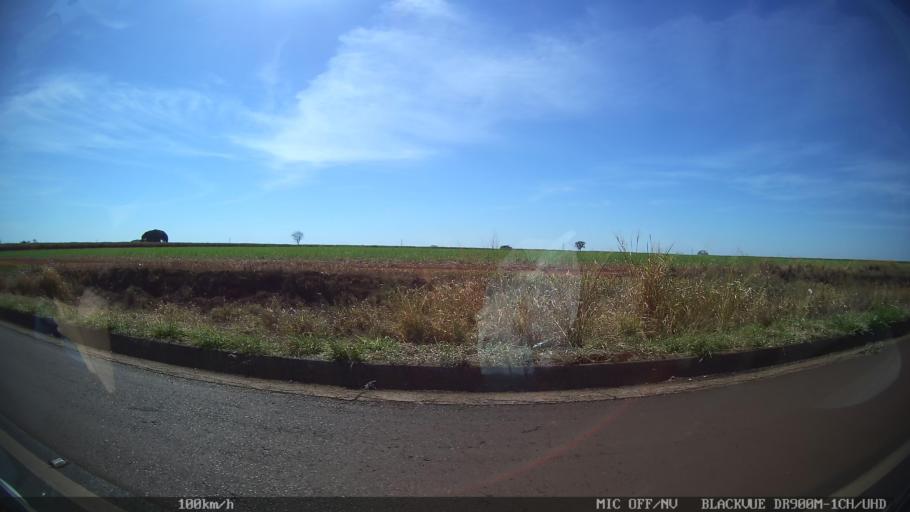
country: BR
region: Sao Paulo
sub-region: Ipua
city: Ipua
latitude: -20.4778
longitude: -48.0871
